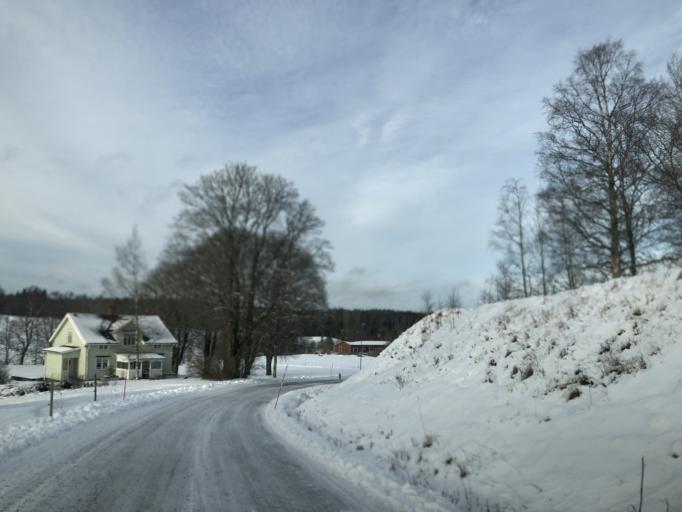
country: SE
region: Vaestra Goetaland
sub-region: Ulricehamns Kommun
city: Ulricehamn
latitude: 57.7873
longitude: 13.5267
